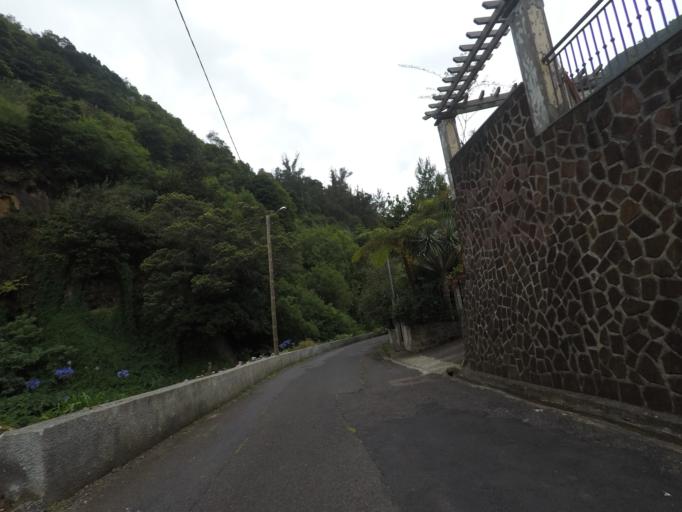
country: PT
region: Madeira
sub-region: Sao Vicente
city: Sao Vicente
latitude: 32.7964
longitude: -17.0439
